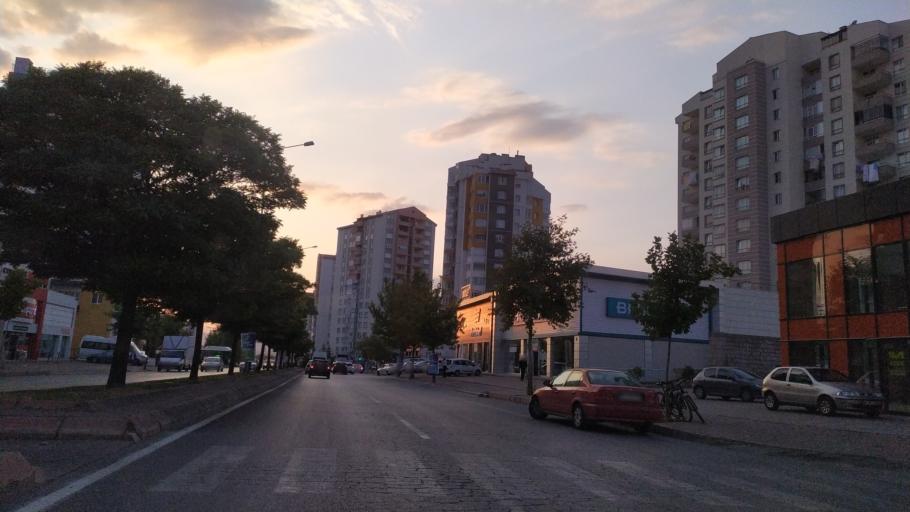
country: TR
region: Kayseri
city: Talas
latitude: 38.7085
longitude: 35.5569
